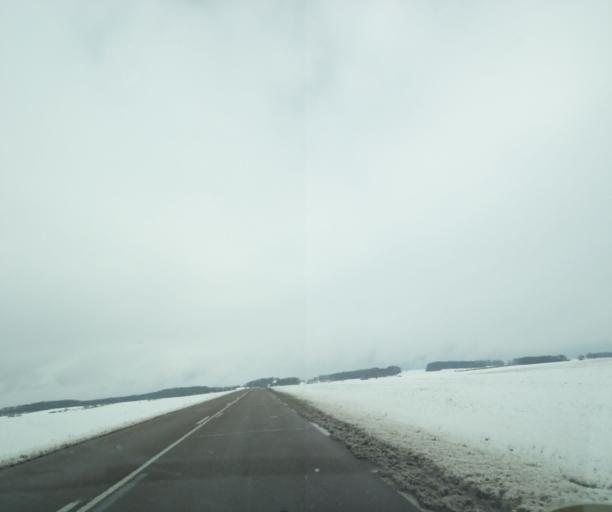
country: FR
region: Champagne-Ardenne
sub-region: Departement de la Haute-Marne
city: Montier-en-Der
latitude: 48.4390
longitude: 4.7301
